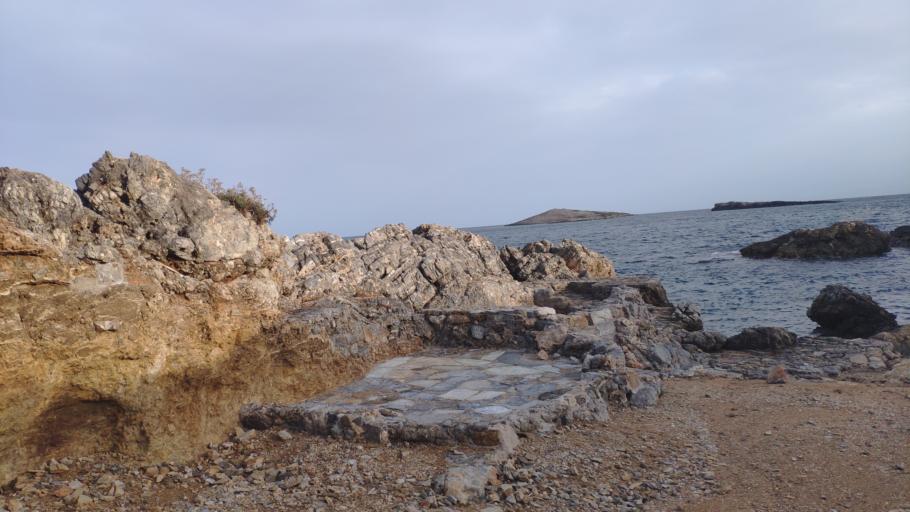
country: GR
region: Attica
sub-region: Nomarchia Anatolikis Attikis
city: Limin Mesoyaias
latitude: 37.9223
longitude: 24.0315
